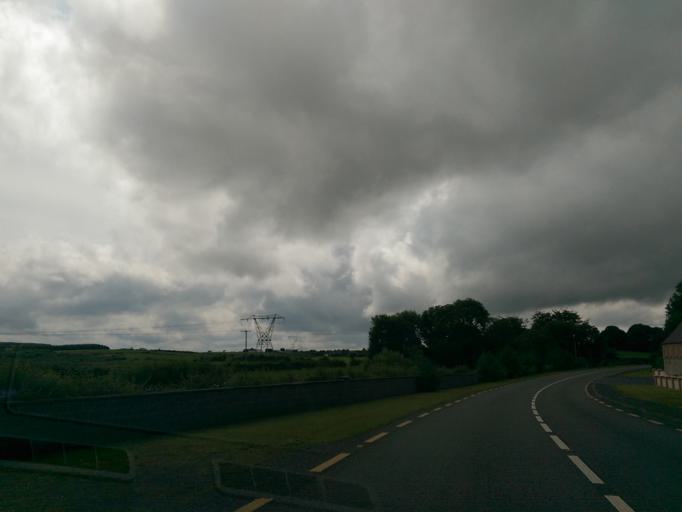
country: IE
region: Munster
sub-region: An Clar
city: Ennis
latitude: 52.7434
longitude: -9.1600
